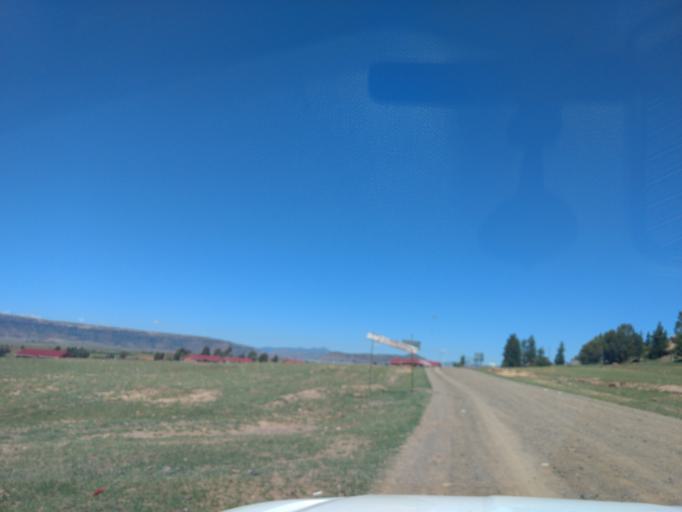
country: LS
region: Maseru
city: Maseru
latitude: -29.4942
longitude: 27.3732
